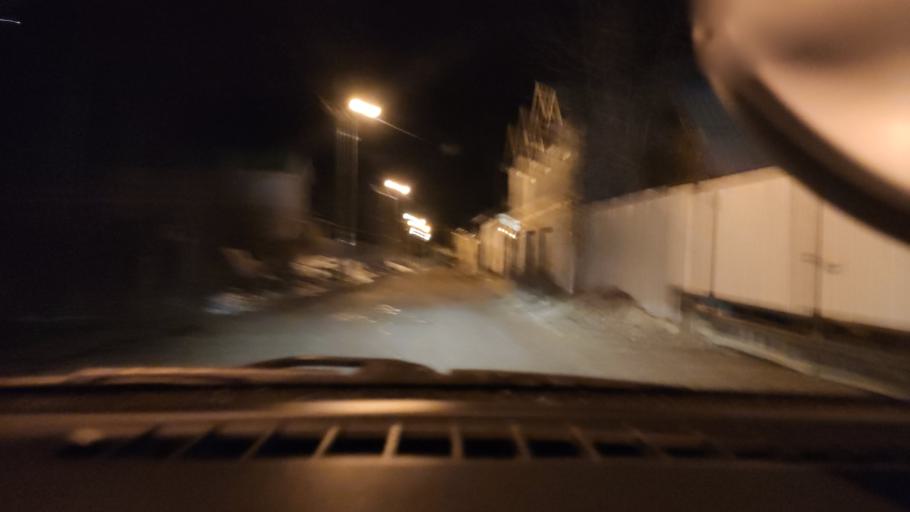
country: RU
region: Samara
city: Samara
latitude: 53.2676
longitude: 50.2327
